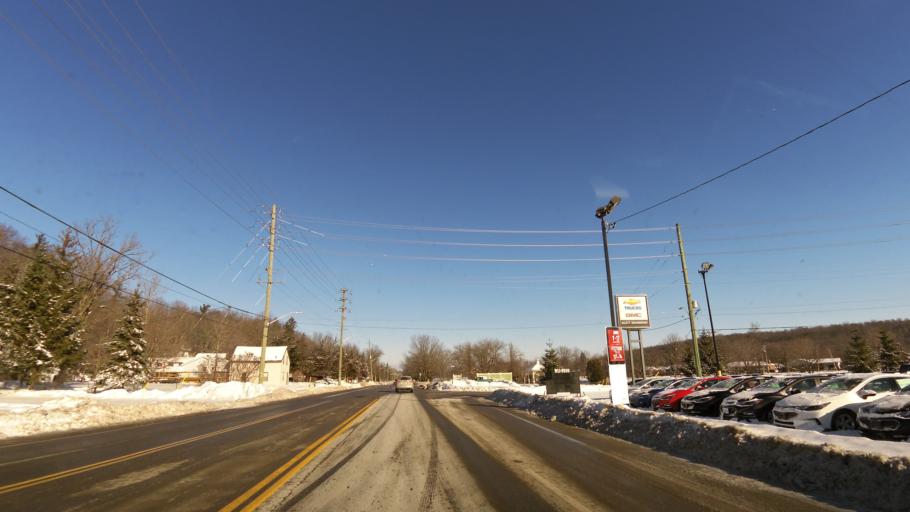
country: CA
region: Ontario
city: Quinte West
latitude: 44.2928
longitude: -77.8074
